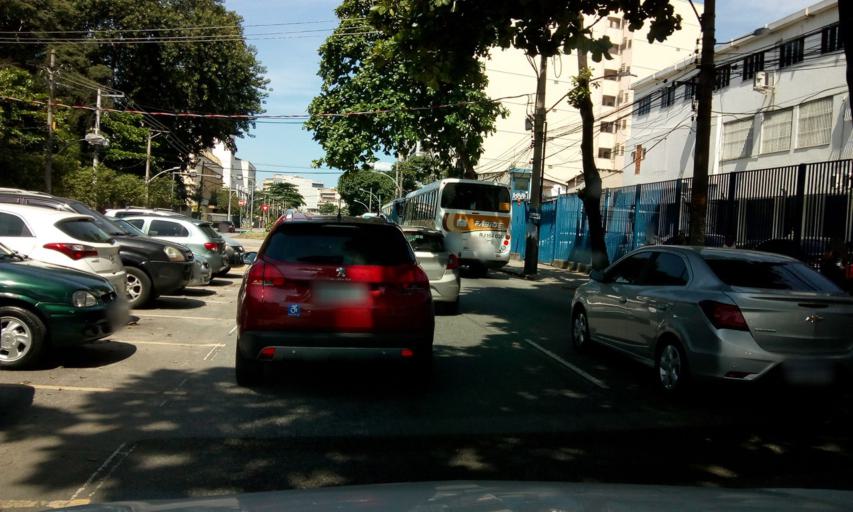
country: BR
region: Rio de Janeiro
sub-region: Rio De Janeiro
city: Rio de Janeiro
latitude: -22.9163
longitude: -43.2391
